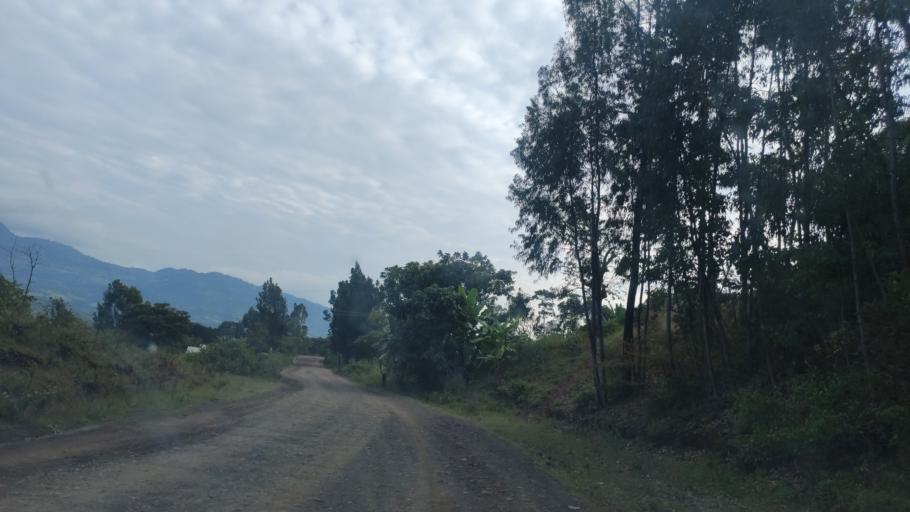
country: ET
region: Southern Nations, Nationalities, and People's Region
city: Arba Minch'
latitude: 6.4423
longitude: 37.3918
